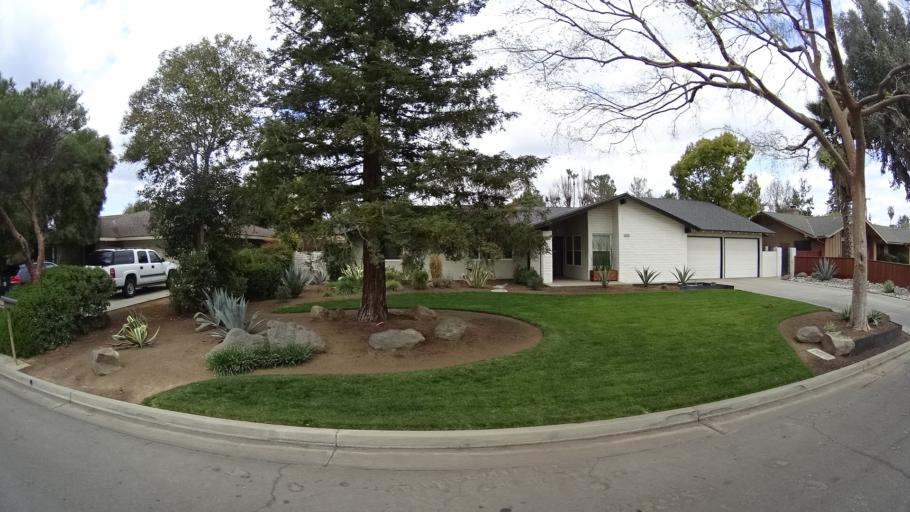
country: US
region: California
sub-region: Fresno County
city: Fresno
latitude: 36.8250
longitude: -119.8428
